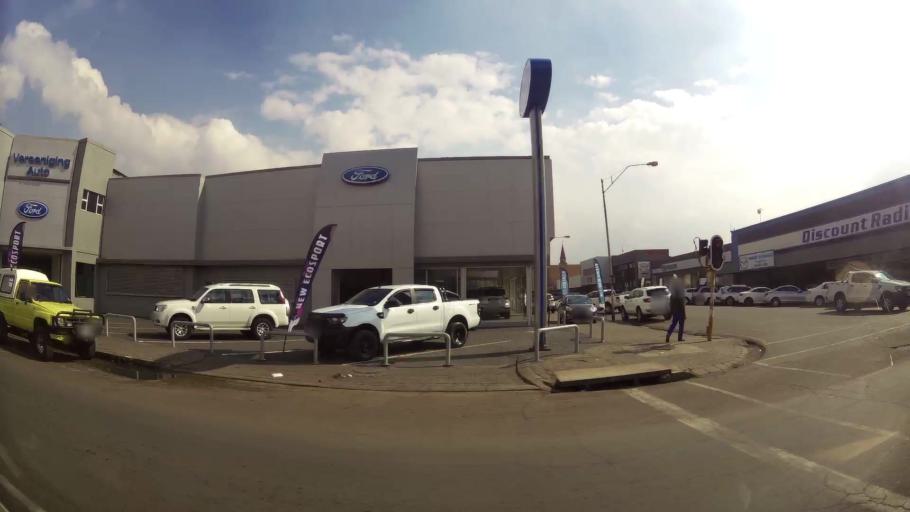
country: ZA
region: Gauteng
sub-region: Sedibeng District Municipality
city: Vereeniging
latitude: -26.6713
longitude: 27.9323
